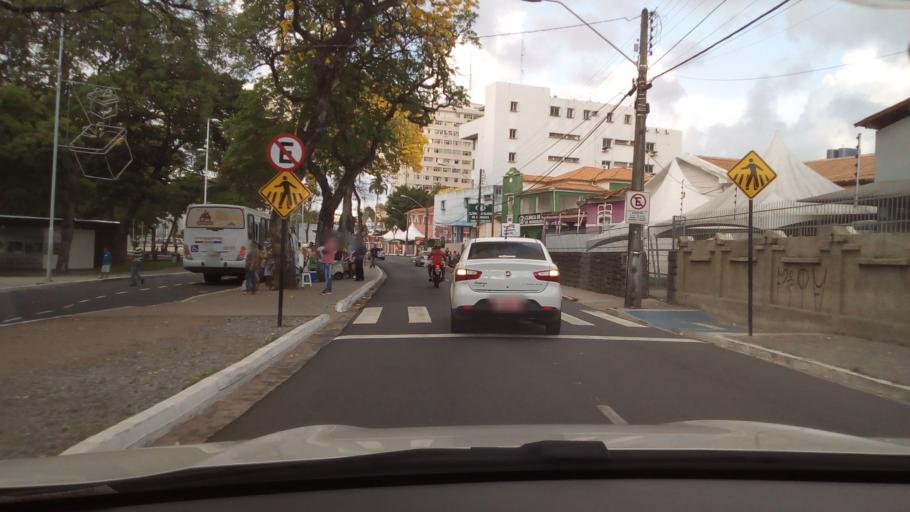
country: BR
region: Paraiba
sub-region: Joao Pessoa
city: Joao Pessoa
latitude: -7.1220
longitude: -34.8791
